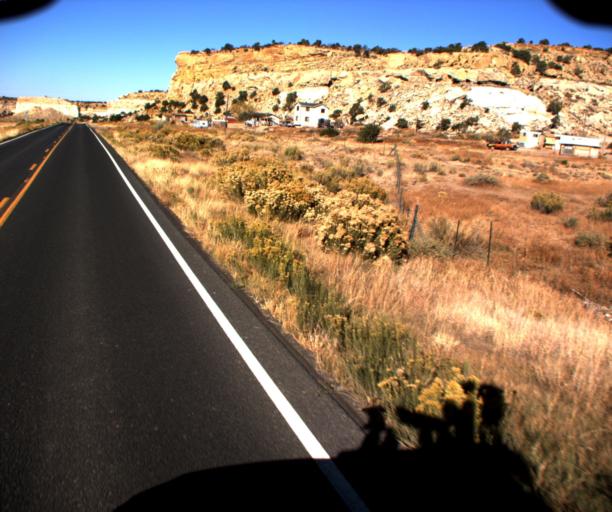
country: US
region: Arizona
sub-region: Apache County
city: Ganado
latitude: 35.7561
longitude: -109.8253
